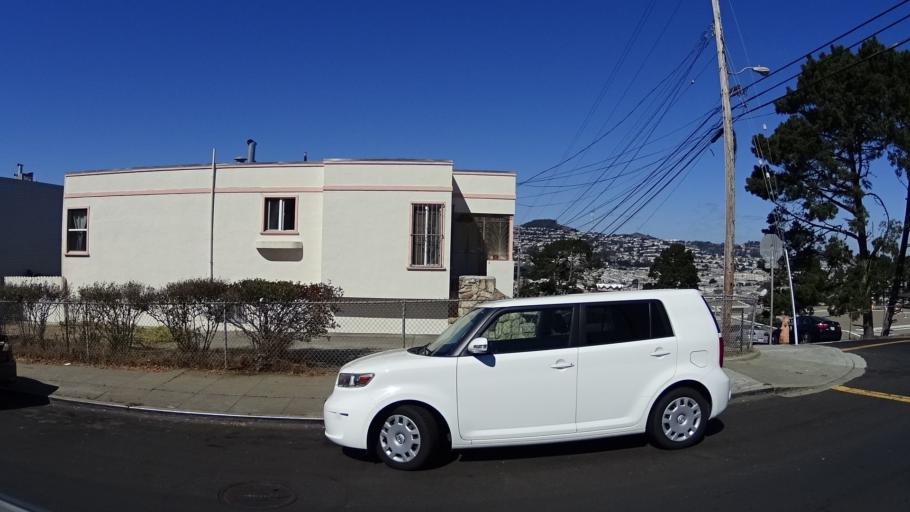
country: US
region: California
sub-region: San Mateo County
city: Daly City
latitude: 37.7065
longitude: -122.4465
